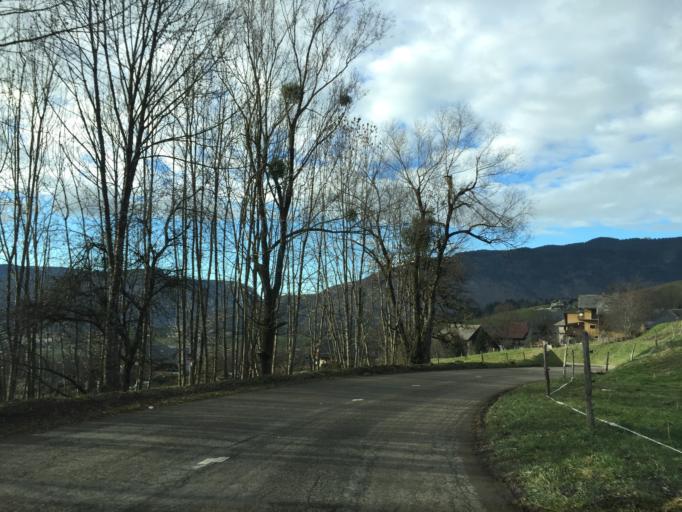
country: FR
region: Rhone-Alpes
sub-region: Departement de la Haute-Savoie
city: Doussard
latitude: 45.7362
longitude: 6.1435
